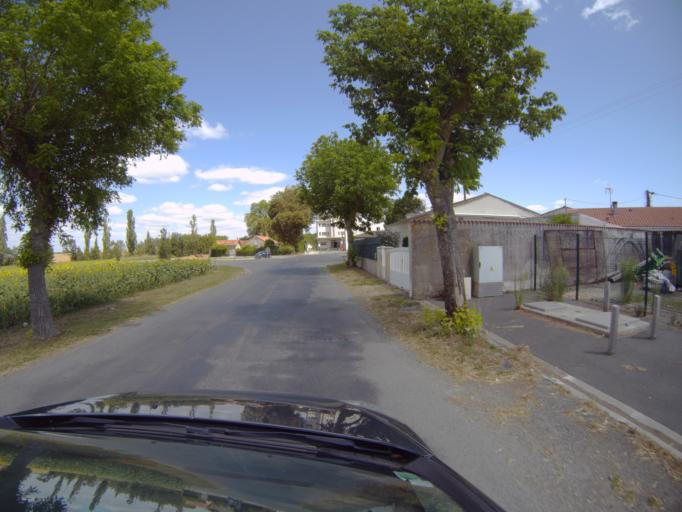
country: FR
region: Poitou-Charentes
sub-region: Departement de la Charente-Maritime
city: Courcon
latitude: 46.2468
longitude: -0.8118
